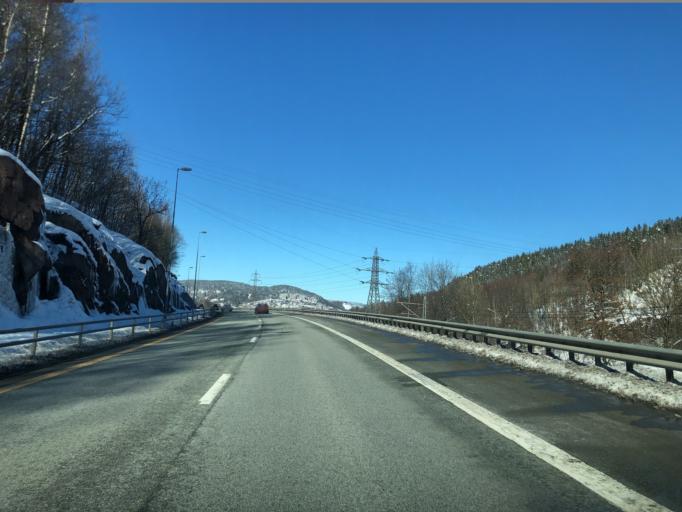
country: NO
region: Buskerud
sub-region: Drammen
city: Skoger
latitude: 59.7159
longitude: 10.2330
